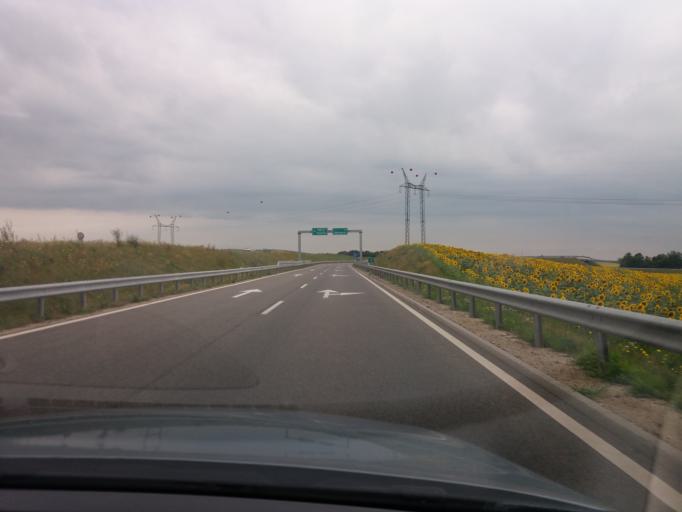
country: HU
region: Fejer
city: Sarszentmihaly
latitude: 47.2113
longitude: 18.3181
